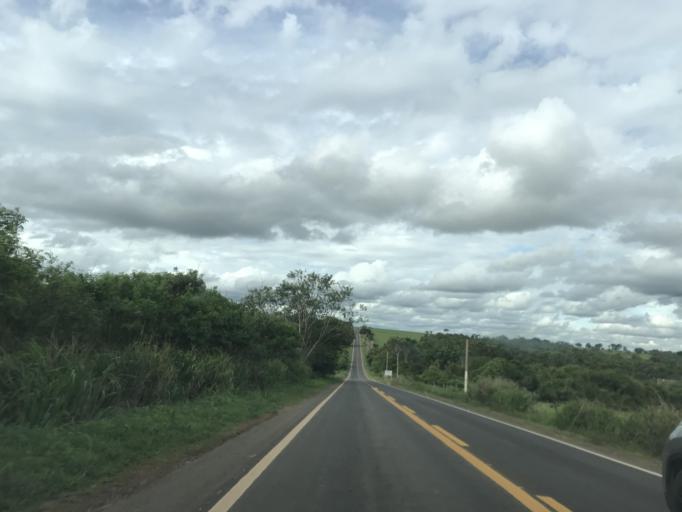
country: BR
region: Goias
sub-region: Piracanjuba
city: Piracanjuba
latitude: -17.1970
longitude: -48.6995
